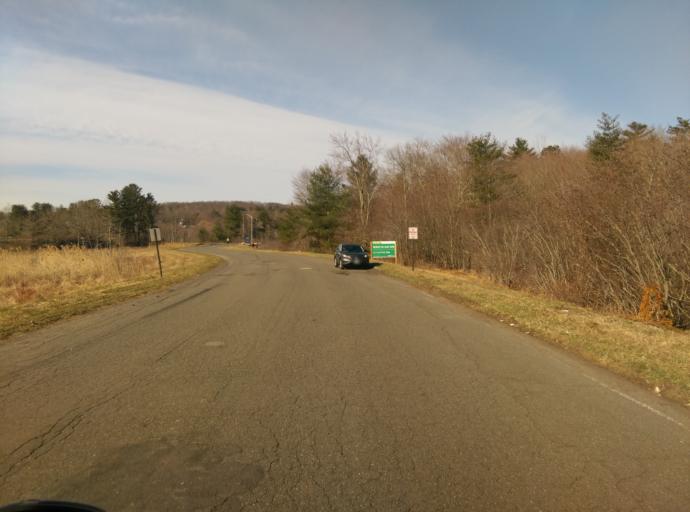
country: US
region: Massachusetts
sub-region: Essex County
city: Haverhill
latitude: 42.7888
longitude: -71.1221
